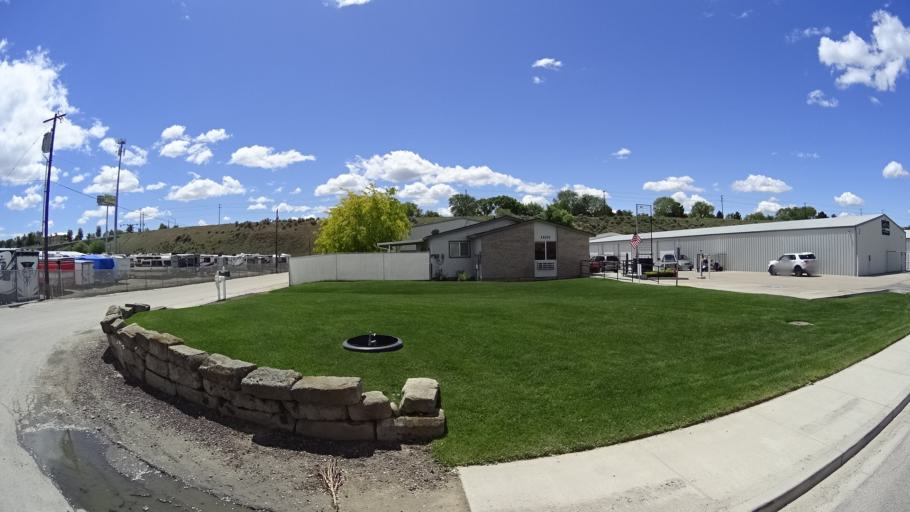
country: US
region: Idaho
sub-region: Ada County
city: Eagle
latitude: 43.6629
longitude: -116.3195
